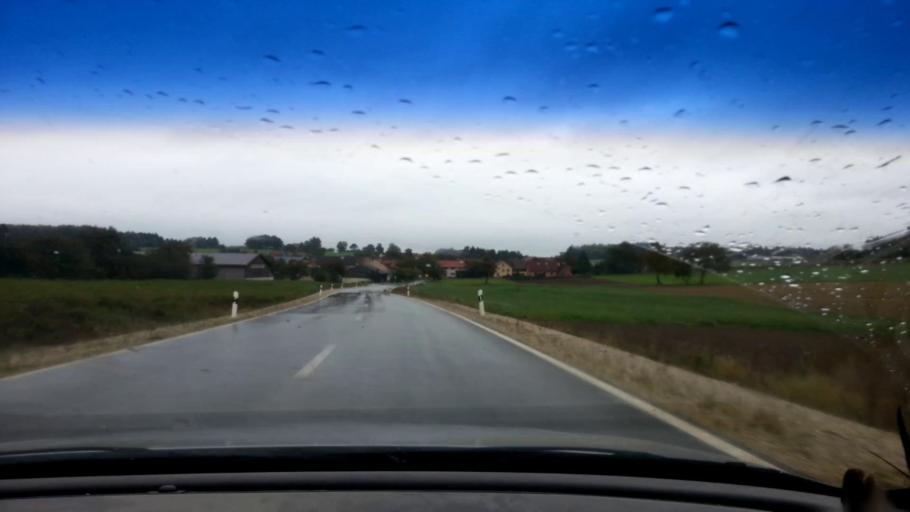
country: DE
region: Bavaria
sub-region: Upper Franconia
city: Poxdorf
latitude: 49.9328
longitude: 11.0801
